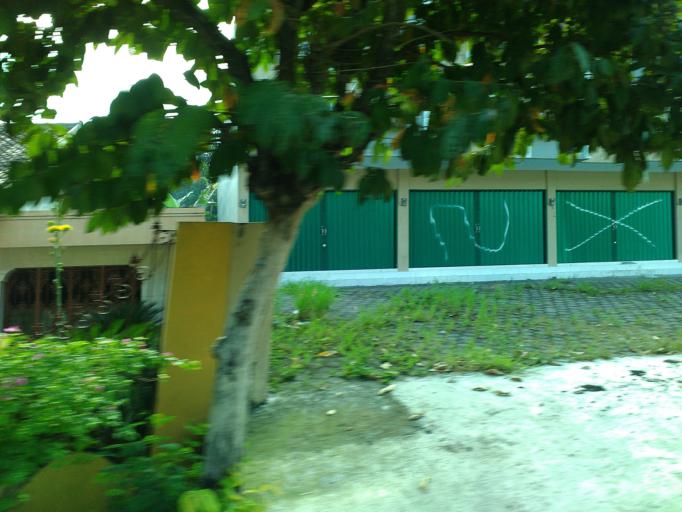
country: ID
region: Central Java
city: Gatak
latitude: -7.6014
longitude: 110.7029
